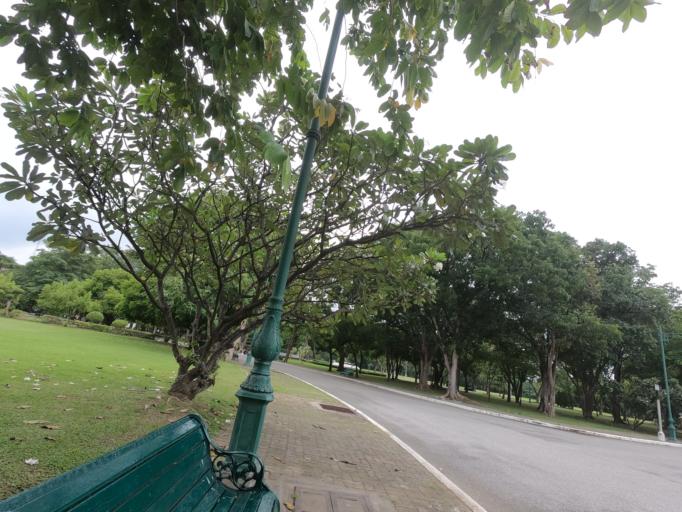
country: TH
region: Nakhon Pathom
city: Nakhon Pathom
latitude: 13.8192
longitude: 100.0458
